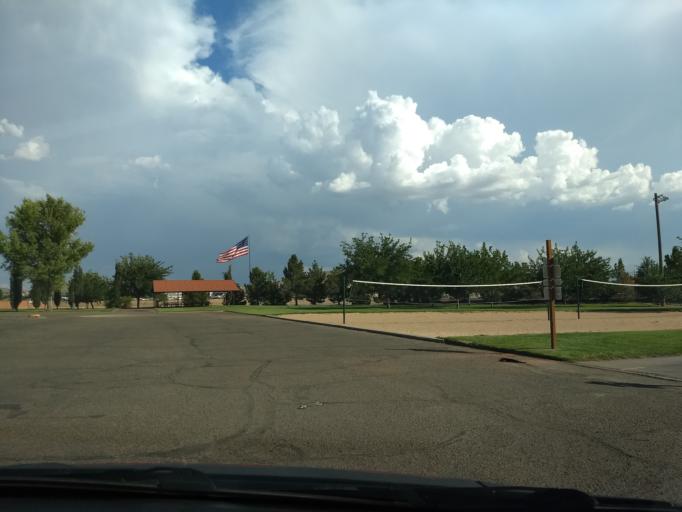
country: US
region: Utah
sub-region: Washington County
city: Saint George
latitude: 37.0906
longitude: -113.5784
